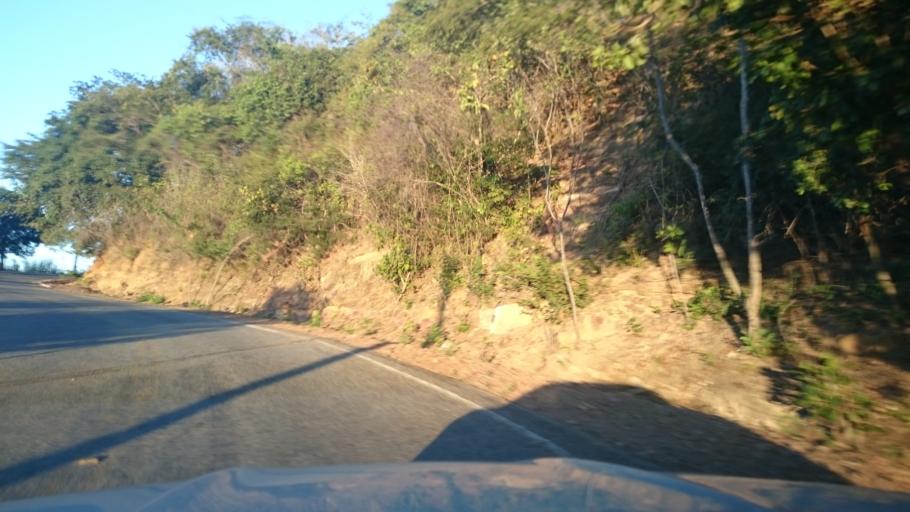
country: BR
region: Rio Grande do Norte
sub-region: Umarizal
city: Umarizal
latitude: -6.0190
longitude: -37.9877
